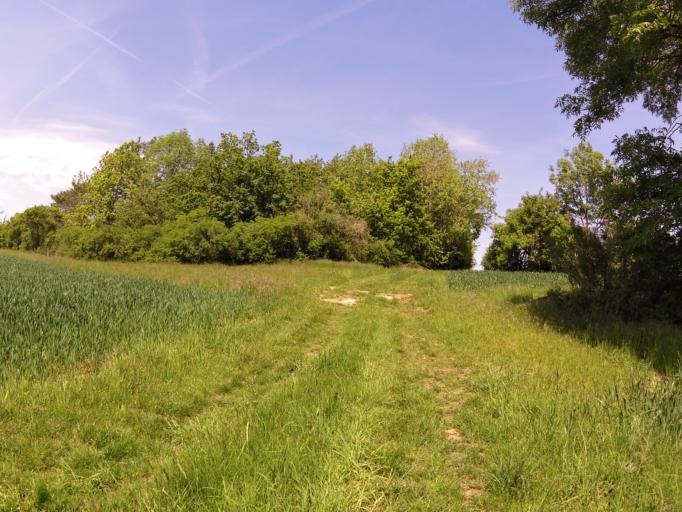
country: DE
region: Bavaria
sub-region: Regierungsbezirk Unterfranken
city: Theilheim
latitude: 49.7360
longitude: 10.0206
